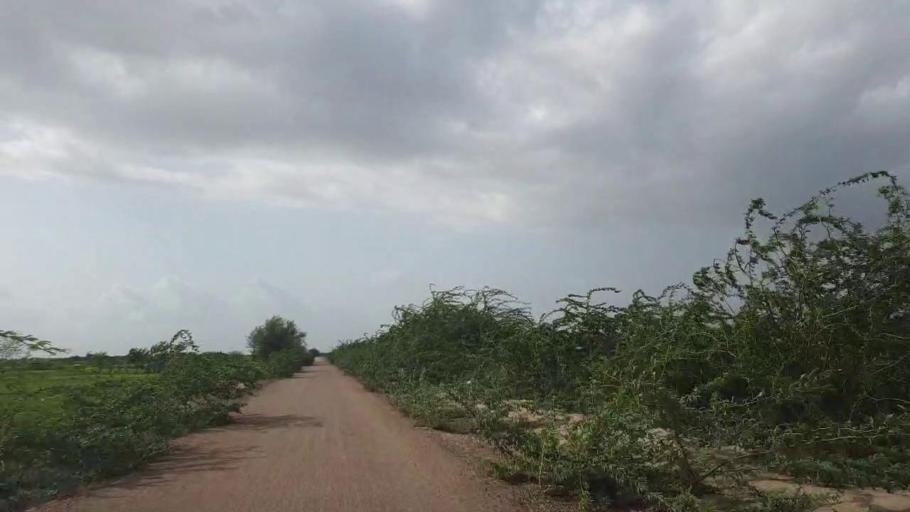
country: PK
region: Sindh
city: Kadhan
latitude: 24.5752
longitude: 69.0601
